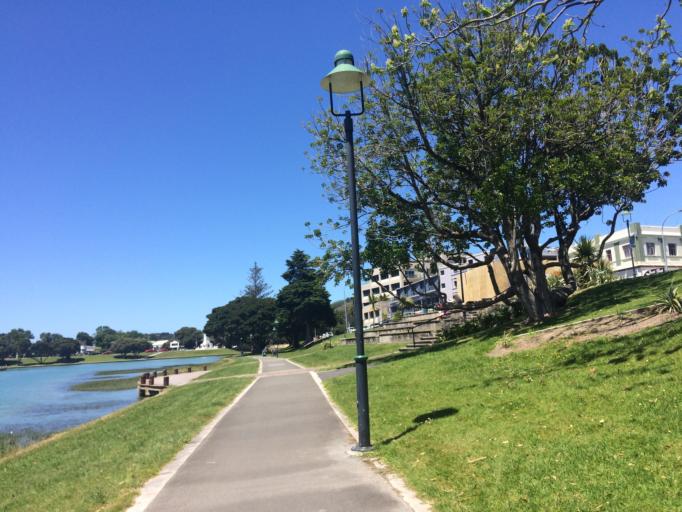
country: NZ
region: Gisborne
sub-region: Gisborne District
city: Gisborne
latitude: -38.6661
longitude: 178.0279
